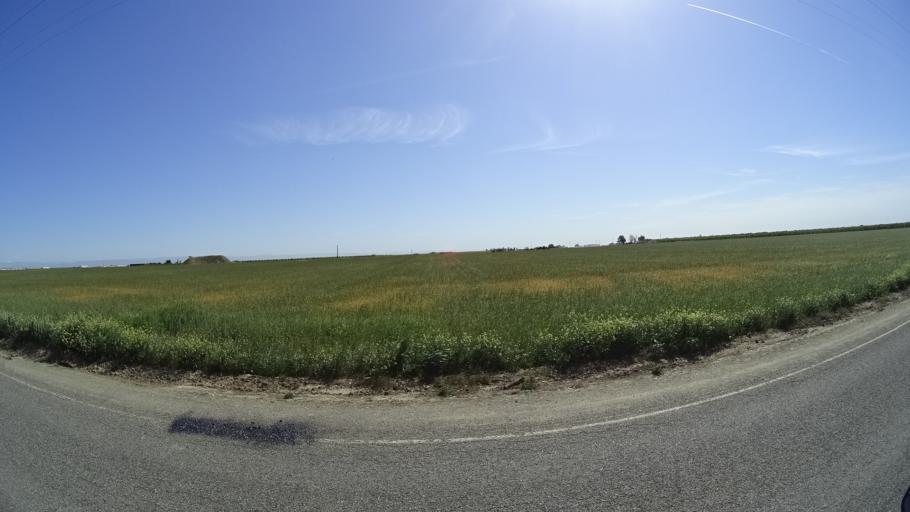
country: US
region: California
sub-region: Glenn County
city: Orland
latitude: 39.6485
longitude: -122.1784
